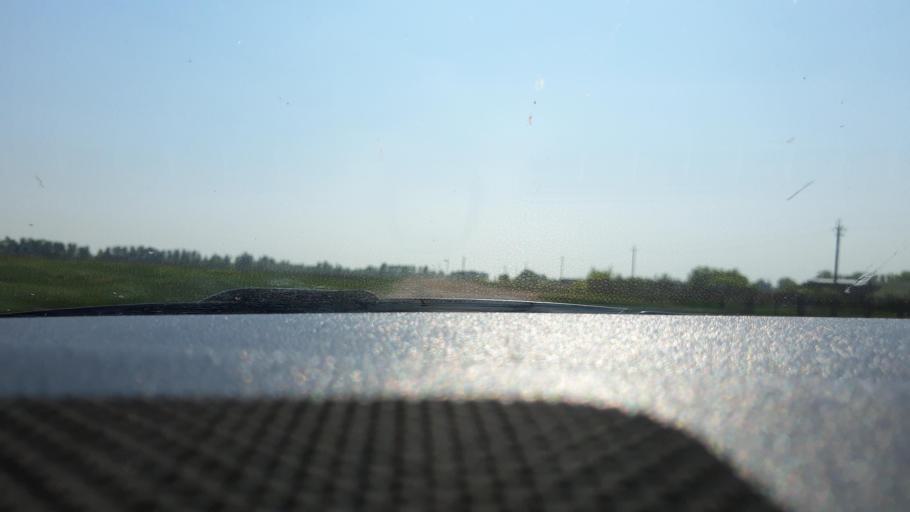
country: RU
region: Bashkortostan
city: Chishmy
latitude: 54.4432
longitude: 55.3143
